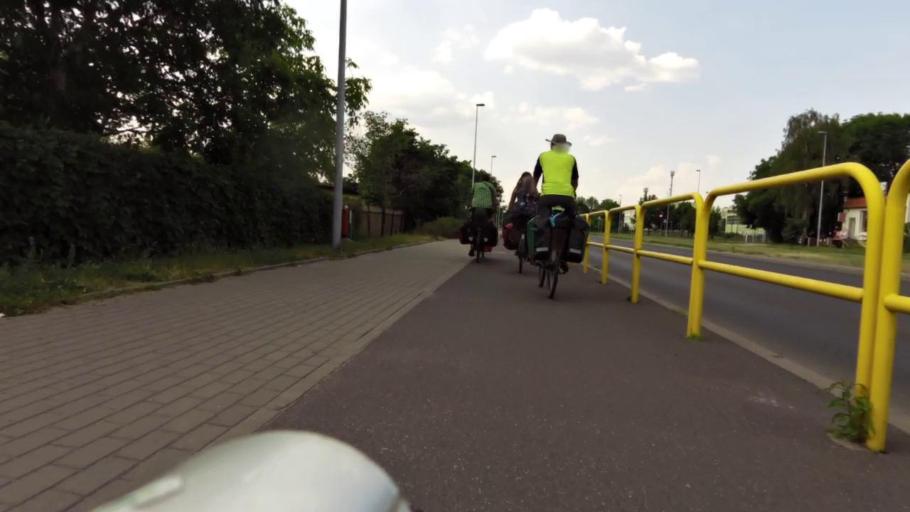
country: PL
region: Kujawsko-Pomorskie
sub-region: Torun
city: Torun
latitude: 53.0436
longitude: 18.5791
